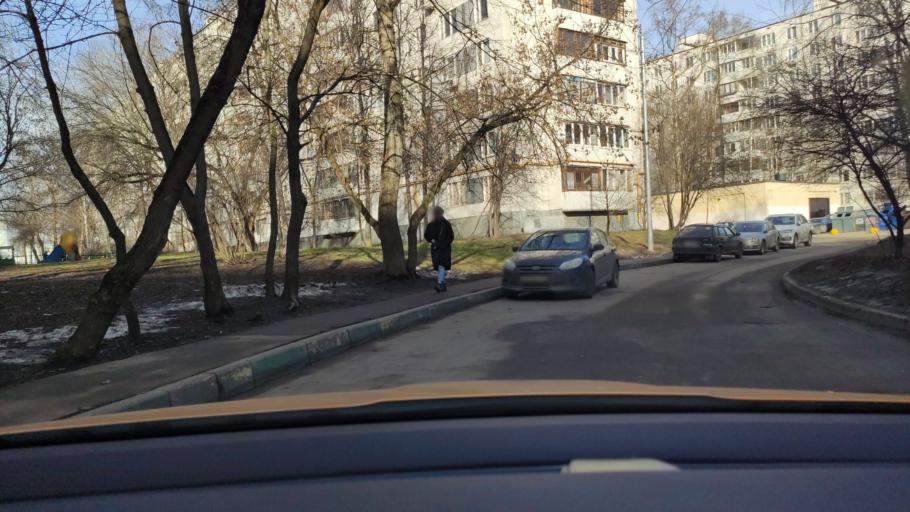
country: RU
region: Moscow
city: Rostokino
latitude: 55.8543
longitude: 37.6863
